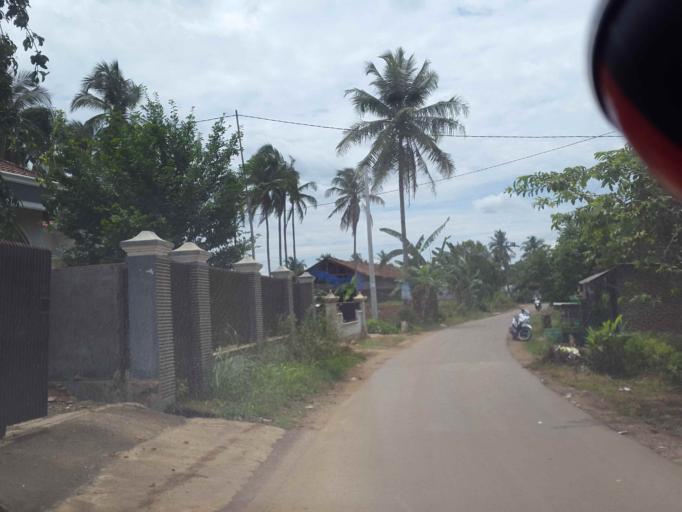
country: ID
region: Lampung
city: Natar
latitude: -5.3239
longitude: 105.1978
